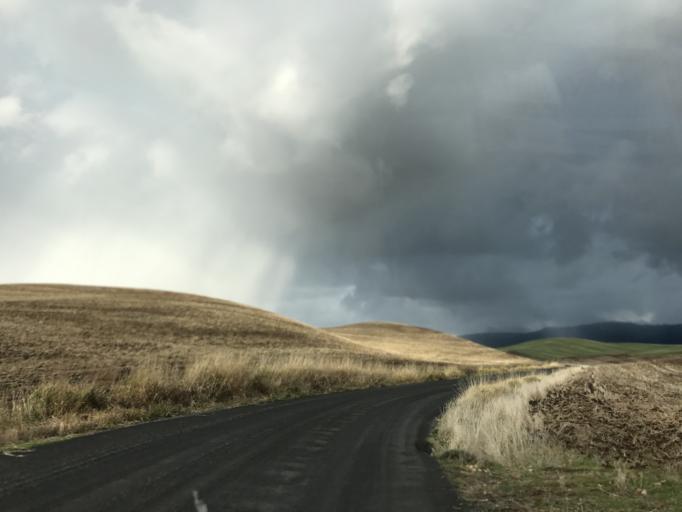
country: US
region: Idaho
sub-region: Latah County
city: Moscow
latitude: 46.7587
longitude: -116.9947
